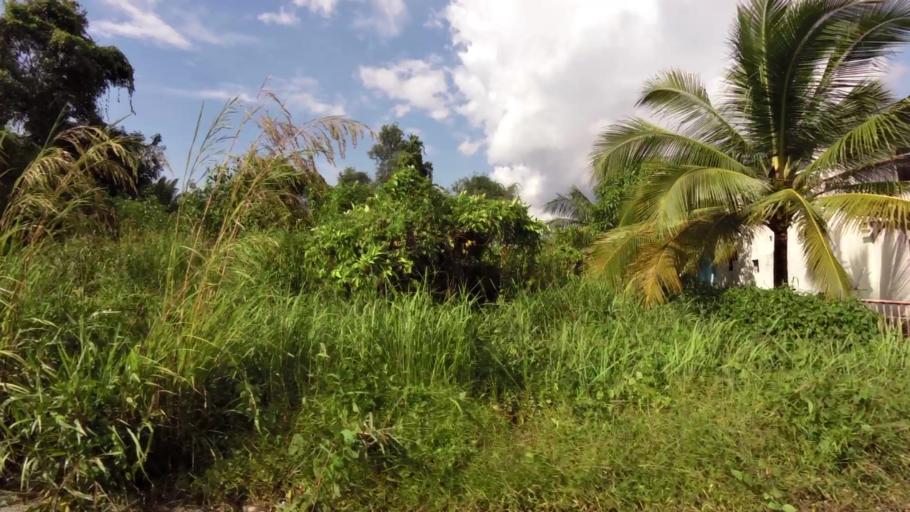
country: BN
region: Brunei and Muara
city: Bandar Seri Begawan
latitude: 4.9533
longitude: 114.9522
